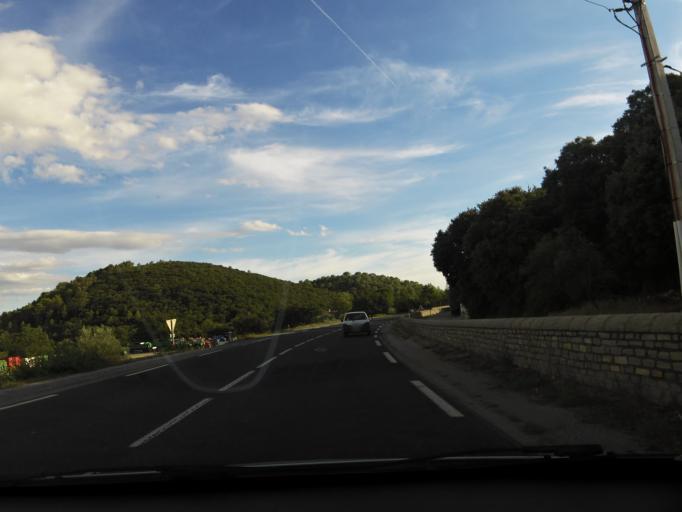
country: FR
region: Languedoc-Roussillon
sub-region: Departement de l'Herault
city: Claret
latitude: 43.8625
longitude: 3.9366
